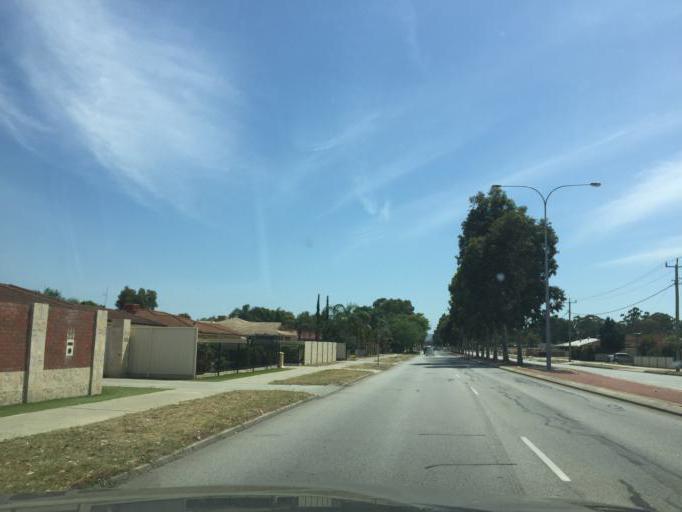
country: AU
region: Western Australia
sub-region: Gosnells
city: Thornlie
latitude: -32.0773
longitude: 115.9585
